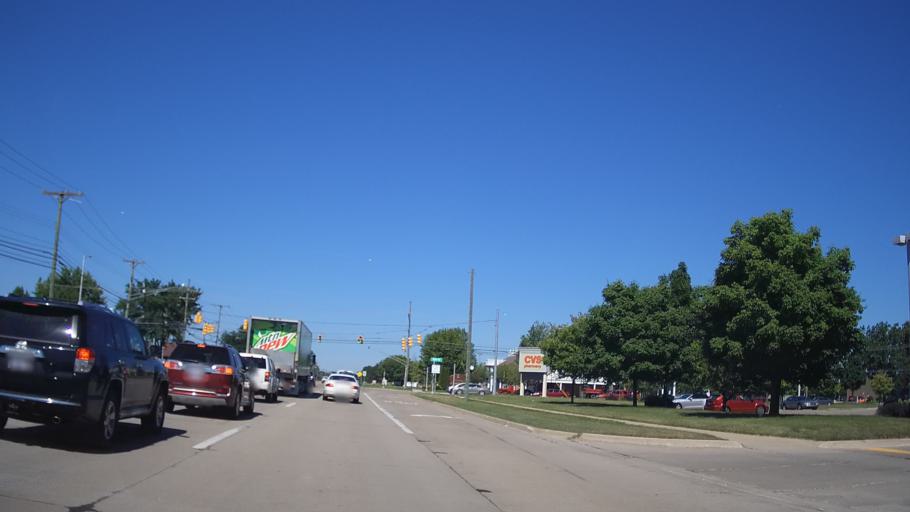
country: US
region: Michigan
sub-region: Macomb County
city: Sterling Heights
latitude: 42.5937
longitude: -83.0696
